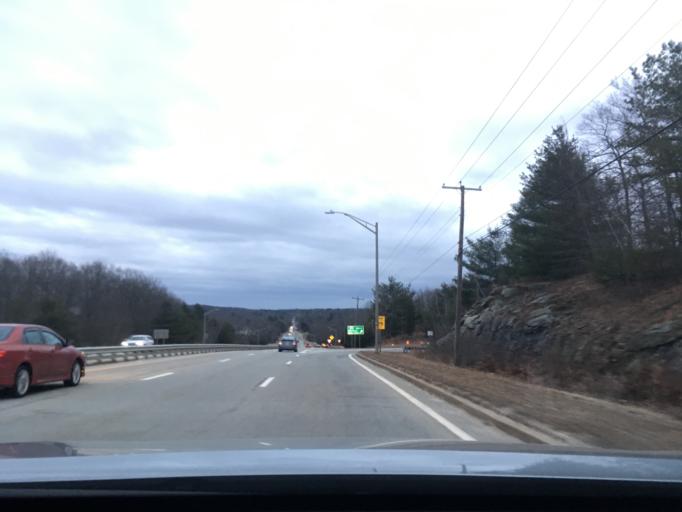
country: US
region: Rhode Island
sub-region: Providence County
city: Smithfield
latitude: 41.9109
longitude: -71.5145
